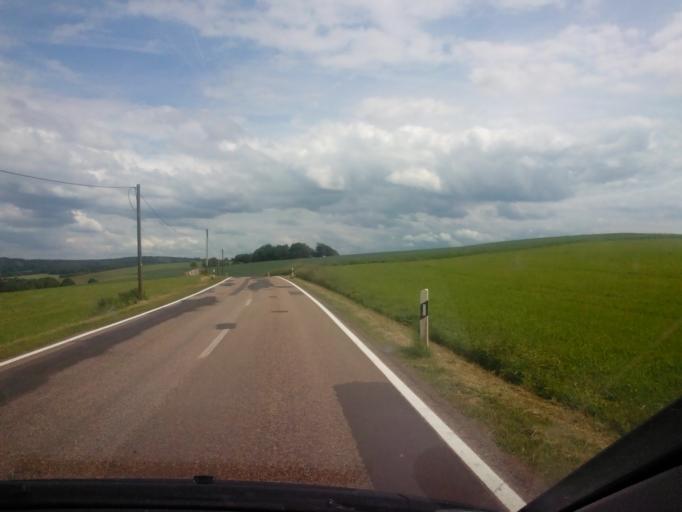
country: DE
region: Saarland
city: Eppelborn
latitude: 49.4327
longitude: 7.0014
